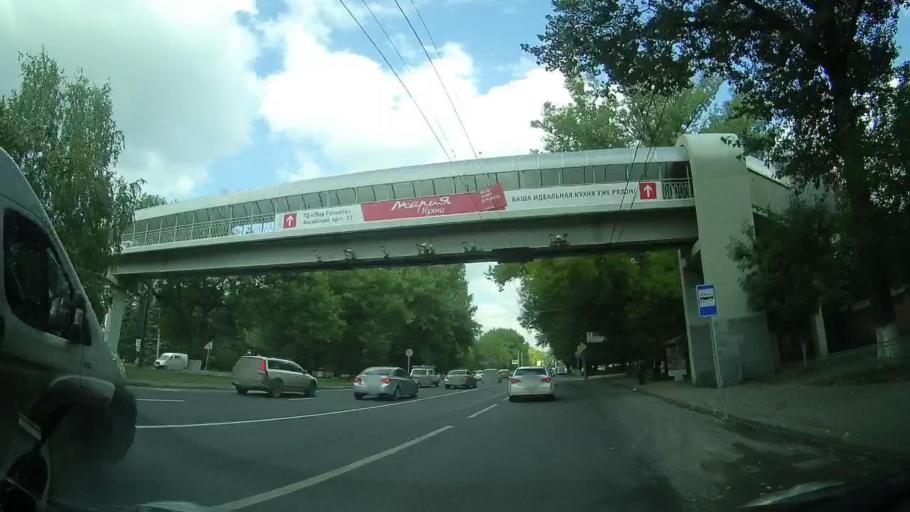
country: RU
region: Rostov
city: Imeni Chkalova
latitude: 47.2560
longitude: 39.7983
